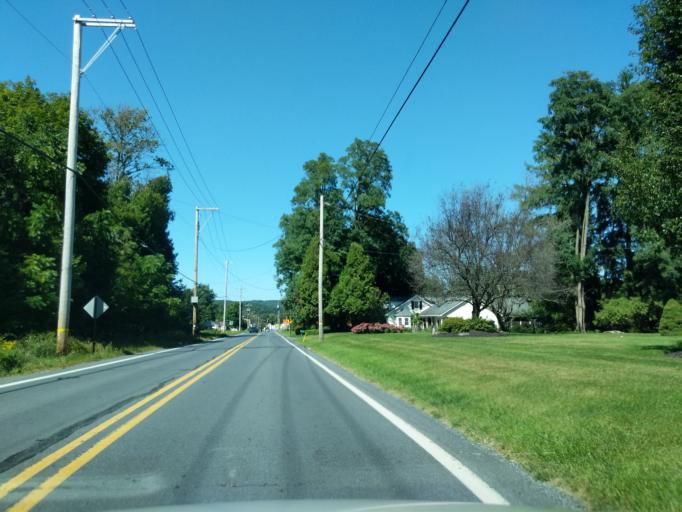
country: US
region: Pennsylvania
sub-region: Lehigh County
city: Coopersburg
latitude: 40.5048
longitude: -75.4451
